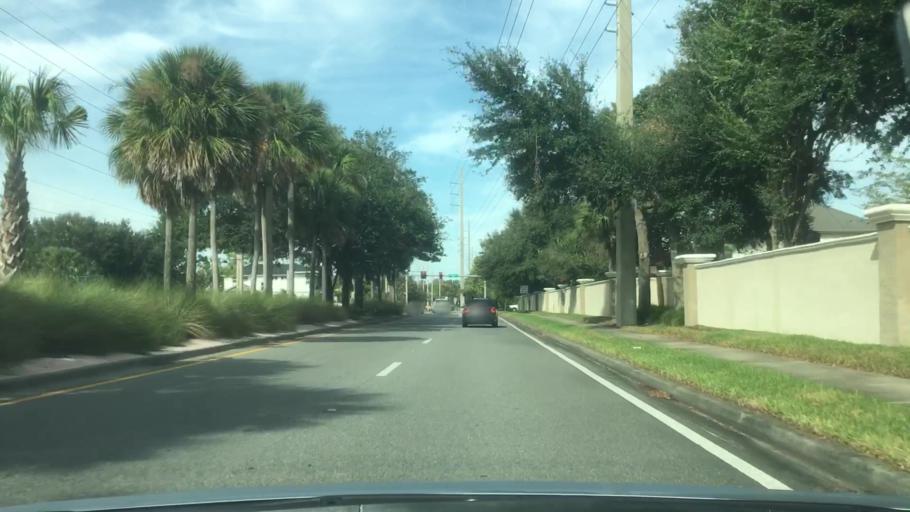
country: US
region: Florida
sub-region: Saint Johns County
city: Ponte Vedra Beach
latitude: 30.2661
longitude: -81.3947
